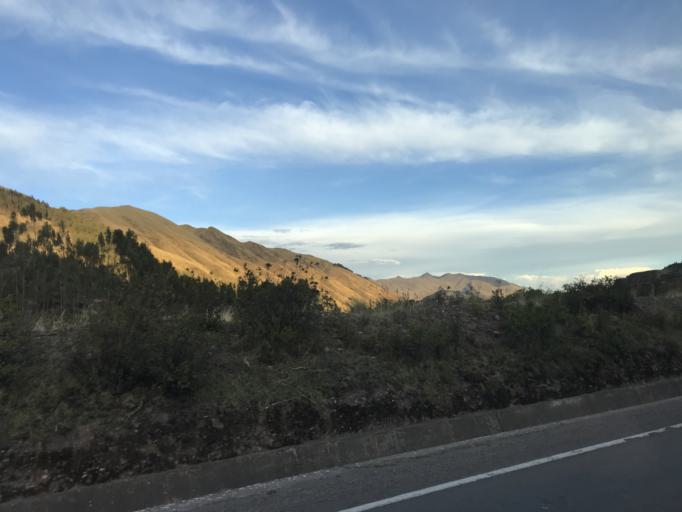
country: PE
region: Cusco
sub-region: Provincia de Cusco
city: Cusco
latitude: -13.4820
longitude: -71.9638
